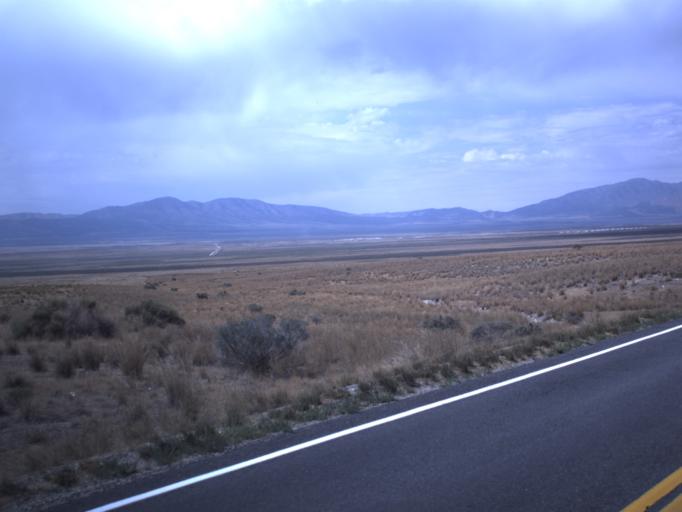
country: US
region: Utah
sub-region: Utah County
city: Eagle Mountain
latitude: 40.2623
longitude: -112.2335
